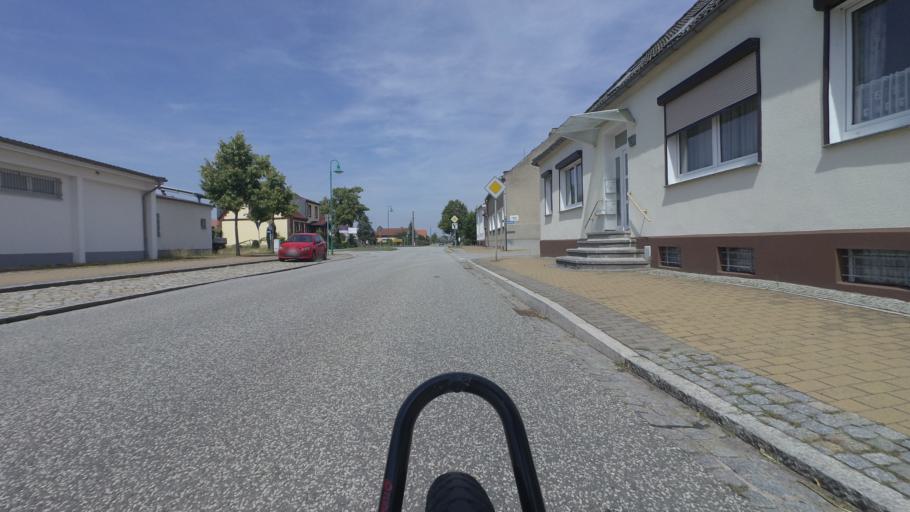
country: DE
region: Brandenburg
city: Rhinow
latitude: 52.7522
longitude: 12.3403
